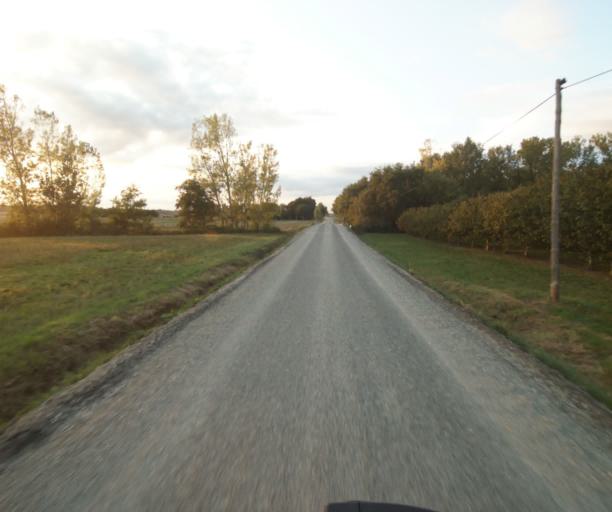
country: FR
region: Midi-Pyrenees
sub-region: Departement du Tarn-et-Garonne
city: Verdun-sur-Garonne
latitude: 43.8328
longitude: 1.2235
